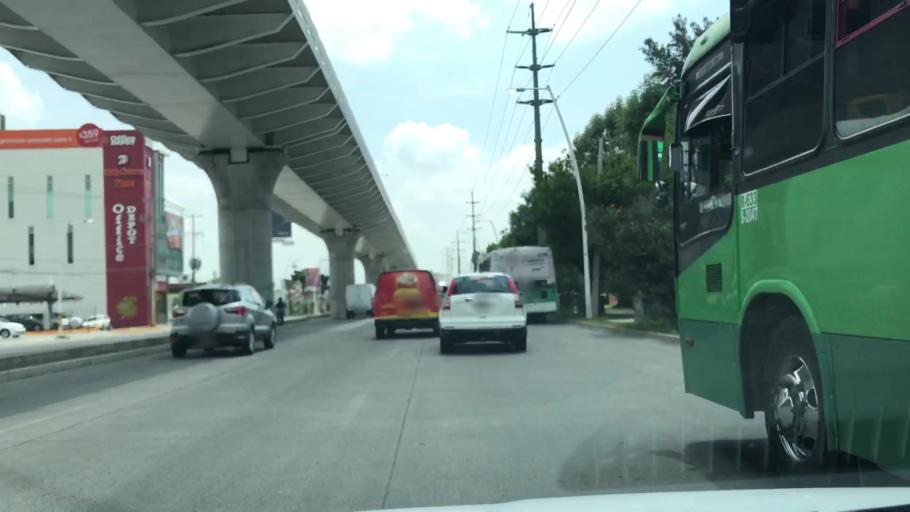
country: MX
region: Jalisco
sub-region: Zapopan
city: Zapopan
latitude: 20.7024
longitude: -103.3598
